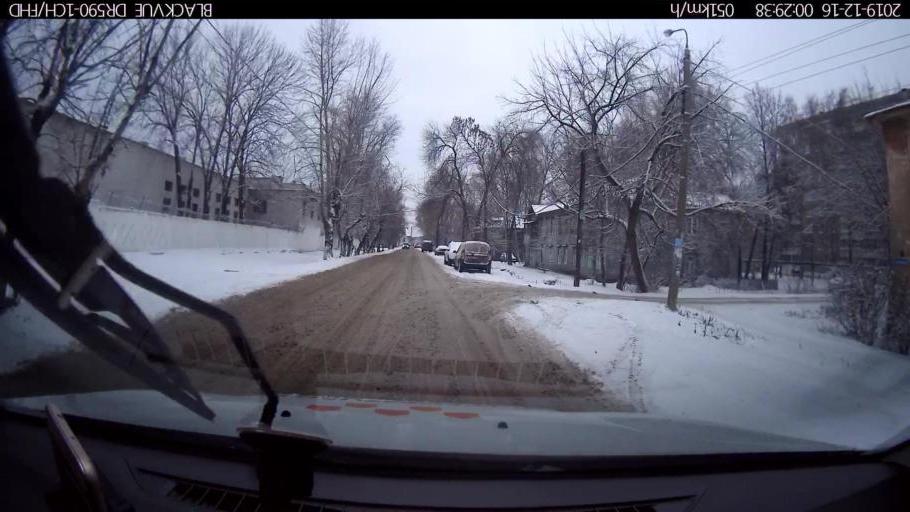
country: RU
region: Nizjnij Novgorod
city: Nizhniy Novgorod
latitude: 56.3112
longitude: 43.8904
